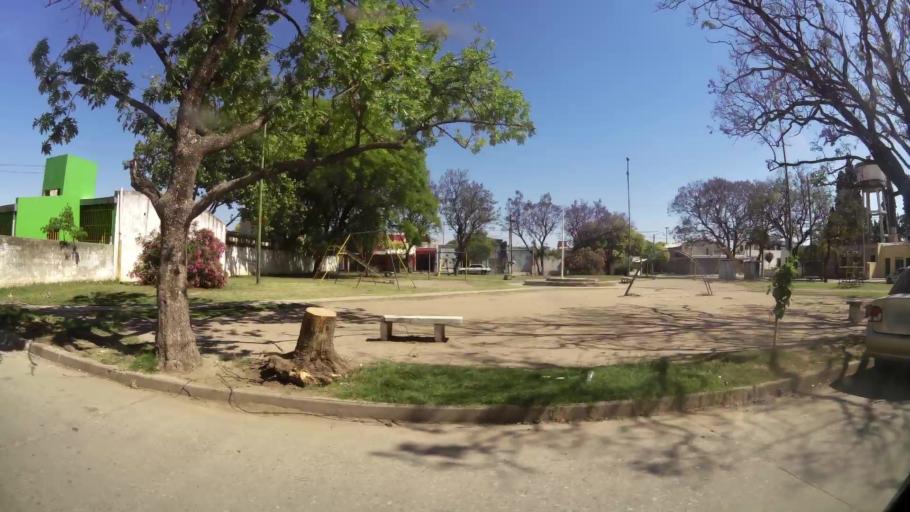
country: AR
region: Cordoba
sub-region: Departamento de Capital
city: Cordoba
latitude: -31.3707
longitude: -64.1362
